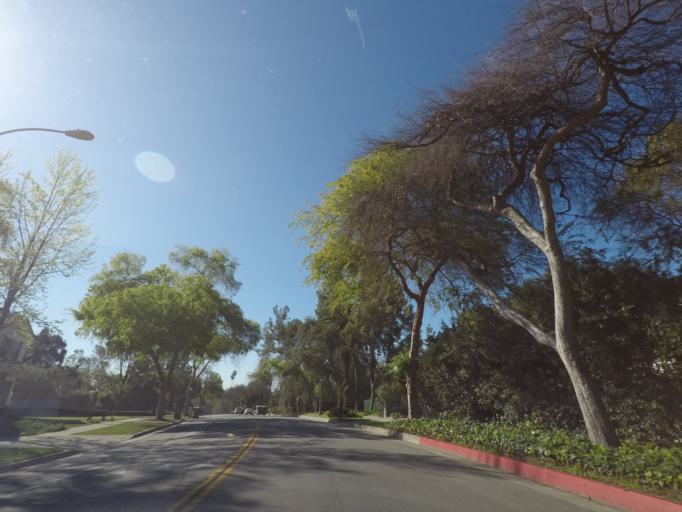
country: US
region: California
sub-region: Los Angeles County
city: La Canada Flintridge
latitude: 34.1675
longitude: -118.1767
